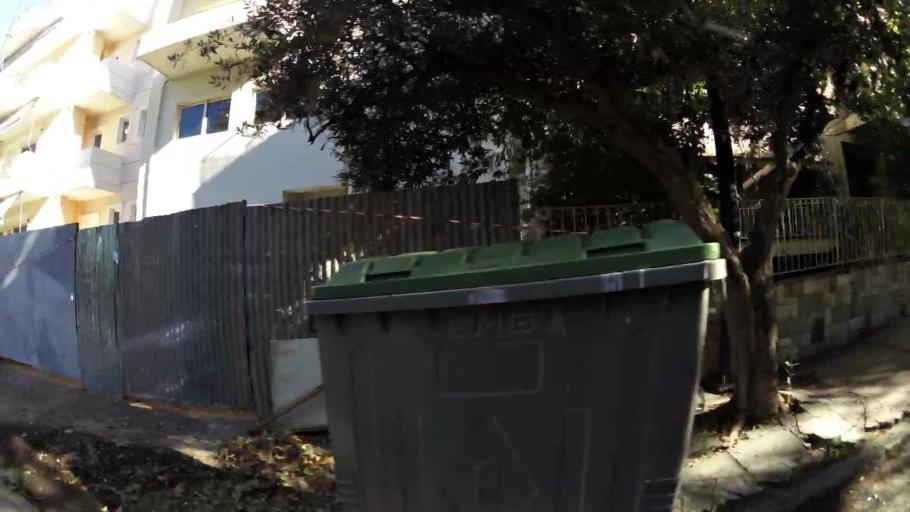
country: GR
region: Attica
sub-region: Nomarchia Athinas
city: Khalandrion
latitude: 38.0264
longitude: 23.7922
